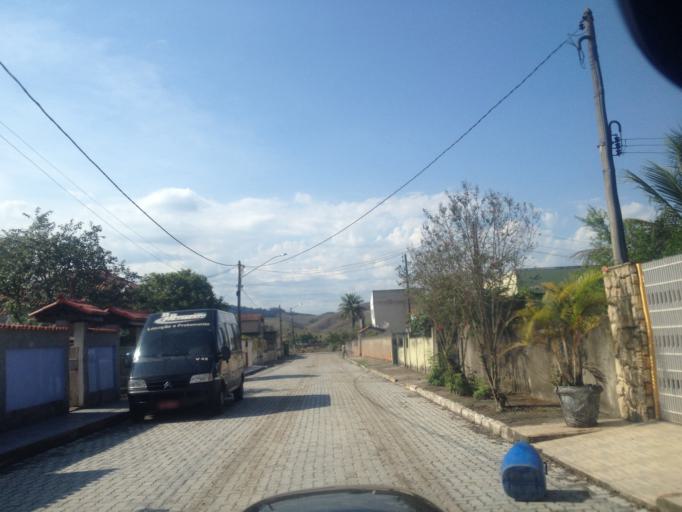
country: BR
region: Rio de Janeiro
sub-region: Porto Real
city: Porto Real
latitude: -22.4230
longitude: -44.2939
